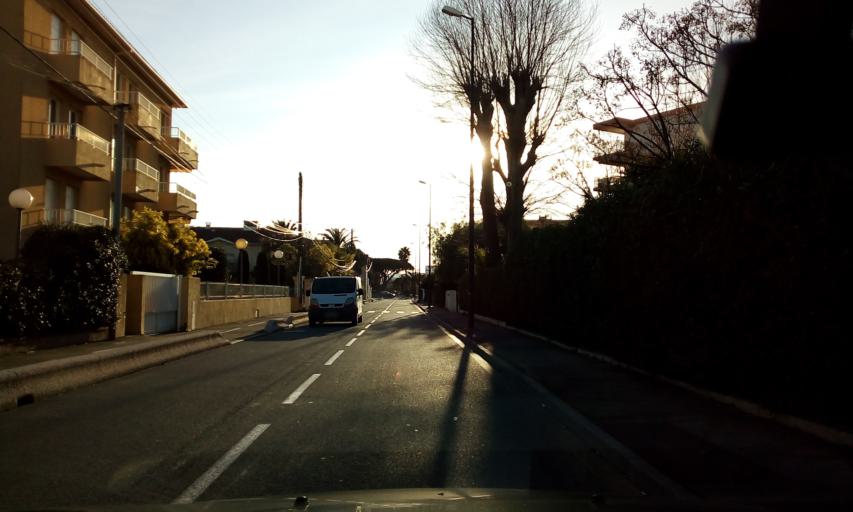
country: FR
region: Provence-Alpes-Cote d'Azur
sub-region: Departement du Var
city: Frejus
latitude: 43.4259
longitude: 6.7479
